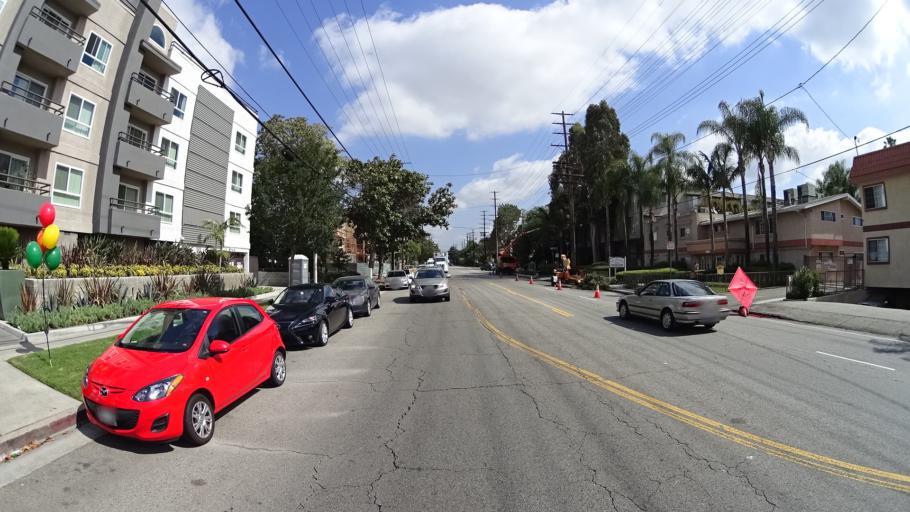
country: US
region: California
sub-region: Los Angeles County
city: Universal City
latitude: 34.1544
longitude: -118.3616
